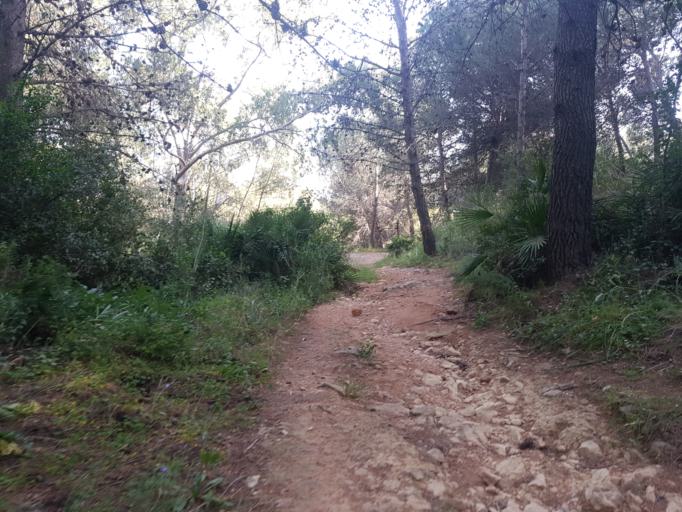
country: ES
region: Andalusia
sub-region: Provincia de Malaga
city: Marbella
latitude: 36.5317
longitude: -4.8764
